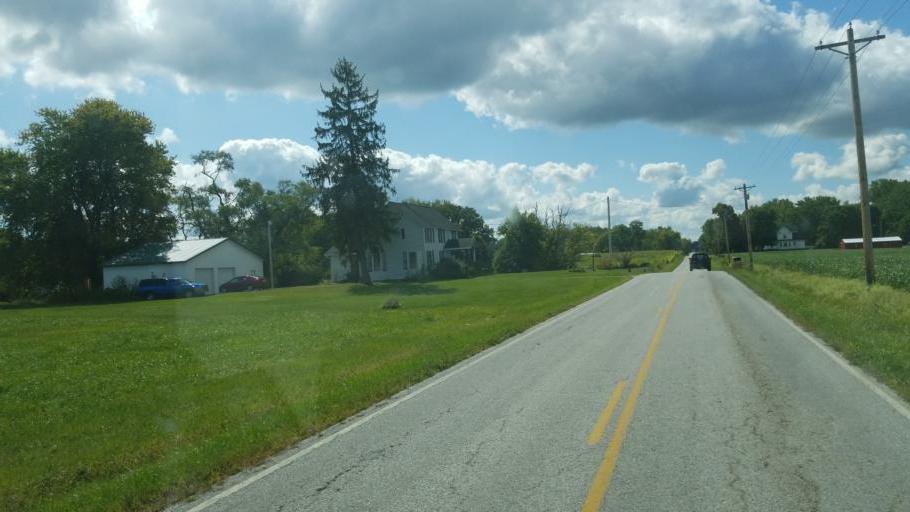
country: US
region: Ohio
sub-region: Lorain County
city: Lagrange
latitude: 41.1235
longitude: -82.0939
